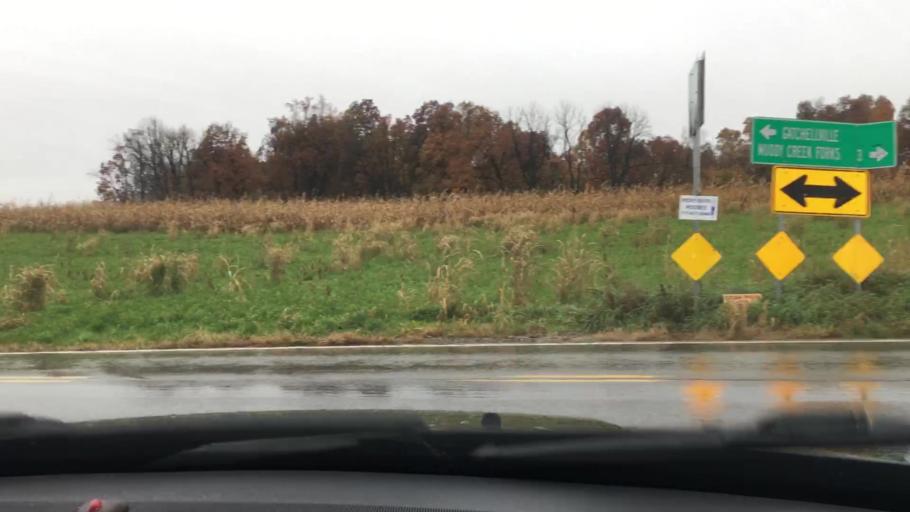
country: US
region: Pennsylvania
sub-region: York County
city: Susquehanna Trails
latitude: 39.7746
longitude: -76.4644
